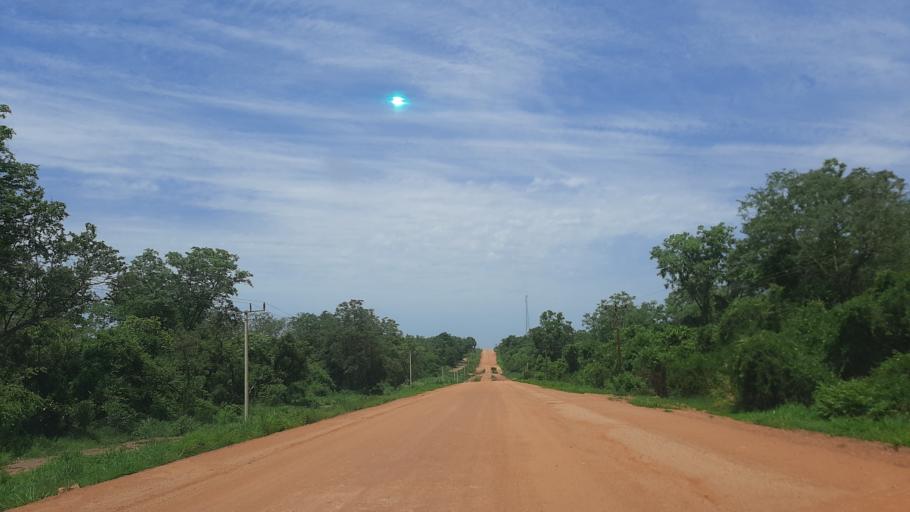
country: ET
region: Gambela
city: Gambela
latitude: 8.0698
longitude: 34.5879
